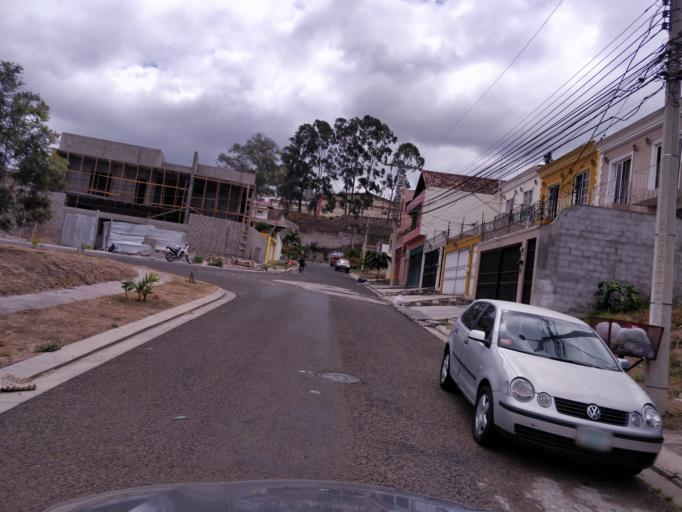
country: HN
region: Francisco Morazan
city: Yaguacire
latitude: 14.0476
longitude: -87.2184
